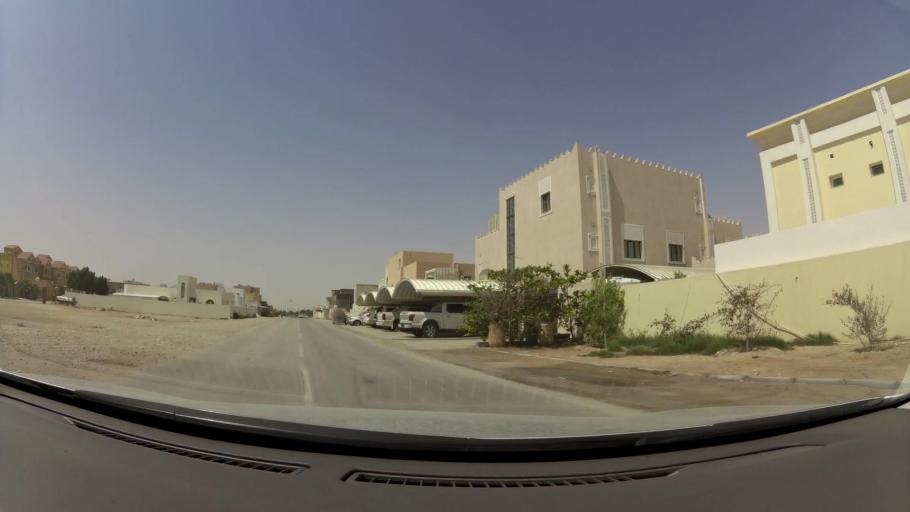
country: QA
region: Baladiyat Umm Salal
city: Umm Salal Muhammad
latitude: 25.3744
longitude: 51.4748
